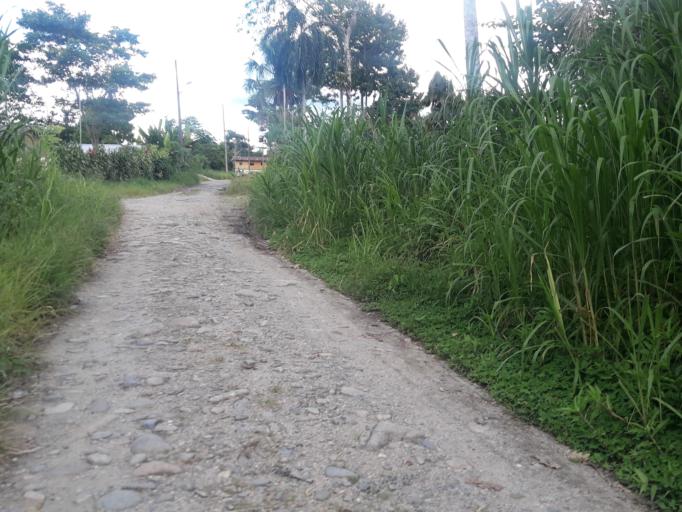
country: EC
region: Napo
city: Tena
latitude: -0.9708
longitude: -77.8401
